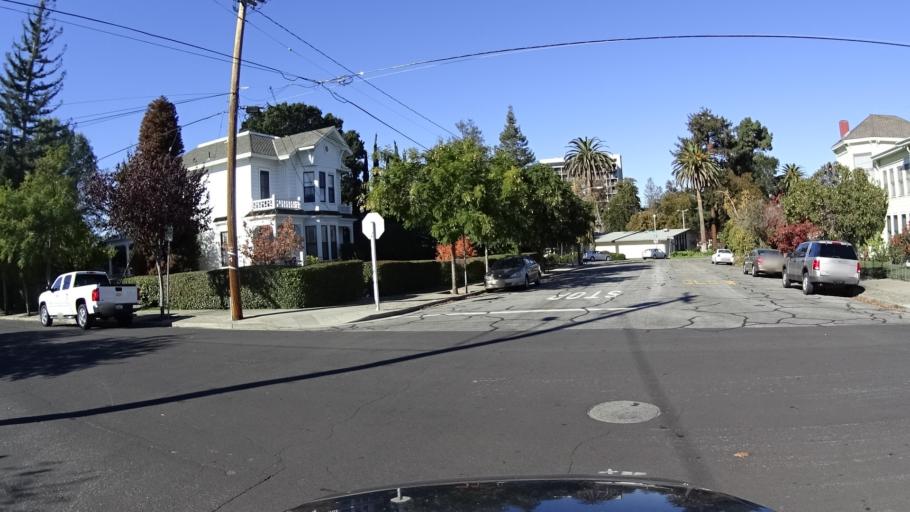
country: US
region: California
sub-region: Santa Clara County
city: Santa Clara
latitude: 37.3465
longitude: -121.9442
